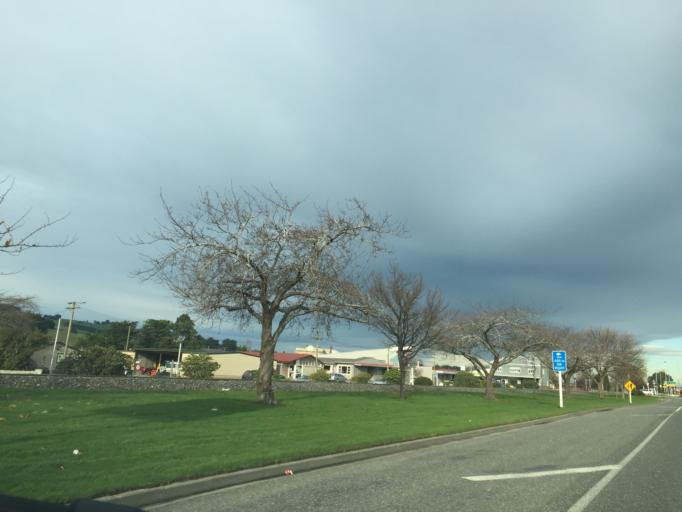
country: NZ
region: Southland
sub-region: Gore District
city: Gore
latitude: -46.1926
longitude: 168.8670
